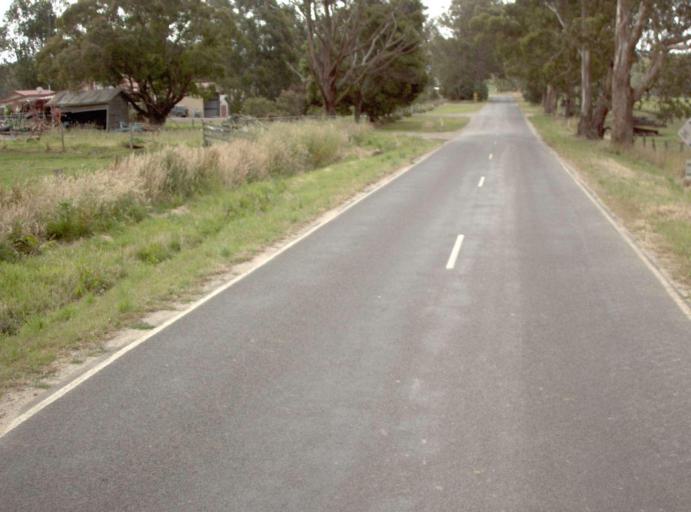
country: AU
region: Victoria
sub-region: Latrobe
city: Traralgon
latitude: -38.3813
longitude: 146.7938
